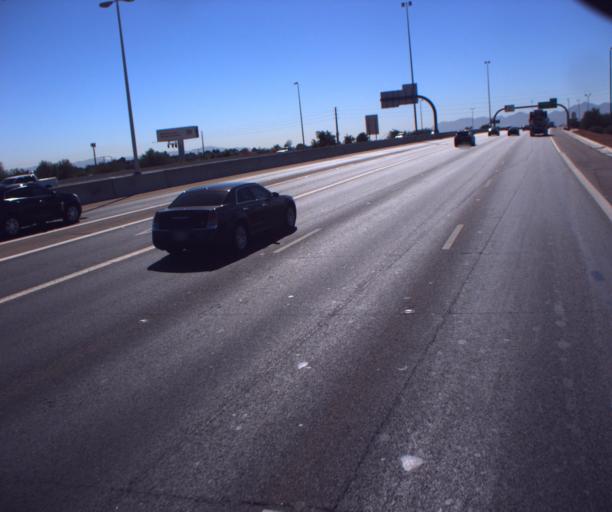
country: US
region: Arizona
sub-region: Maricopa County
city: Peoria
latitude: 33.5259
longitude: -112.2693
